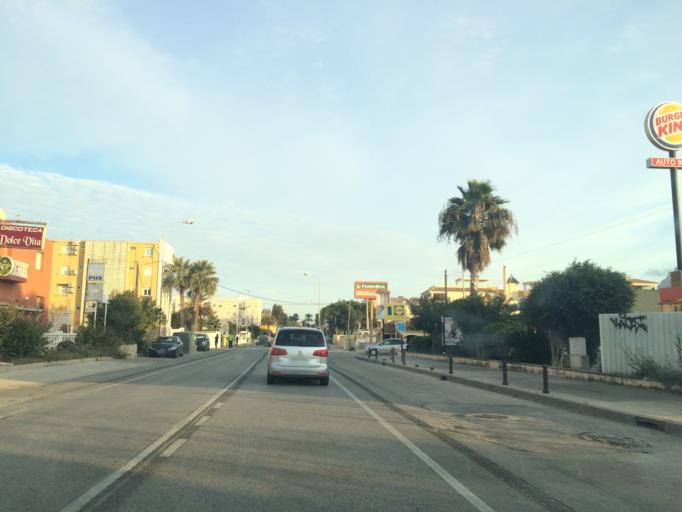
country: ES
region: Valencia
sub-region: Provincia de Alicante
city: Denia
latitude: 38.8497
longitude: 0.0959
